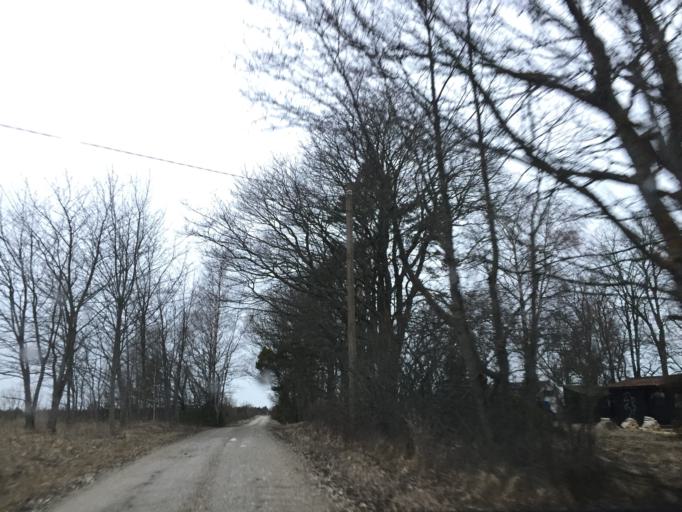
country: EE
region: Laeaene
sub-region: Haapsalu linn
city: Haapsalu
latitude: 58.6852
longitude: 23.5075
